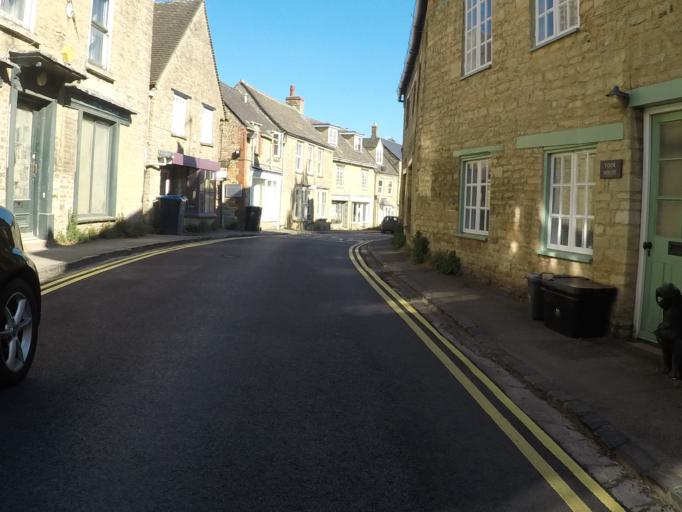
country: GB
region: England
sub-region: Oxfordshire
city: Charlbury
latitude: 51.8725
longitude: -1.4821
